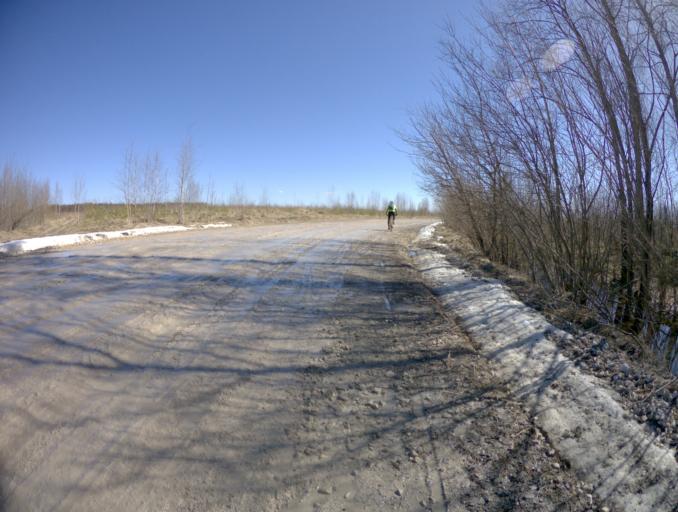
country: RU
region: Vladimir
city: Orgtrud
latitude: 56.3157
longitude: 40.7488
